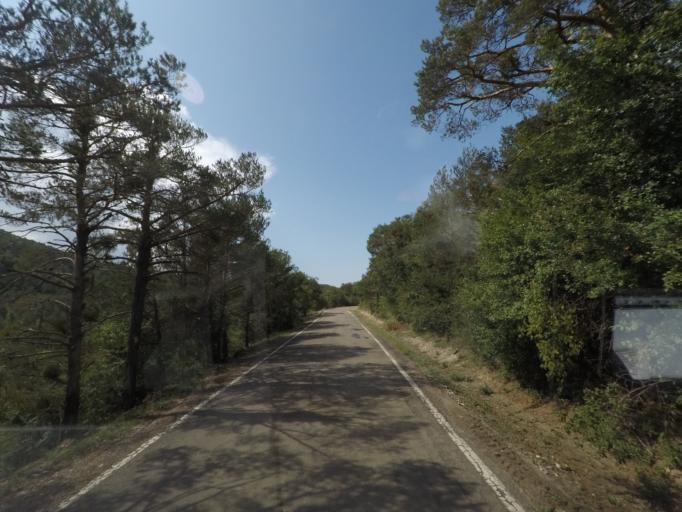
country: ES
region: Aragon
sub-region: Provincia de Huesca
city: Yebra de Basa
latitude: 42.3971
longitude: -0.3492
